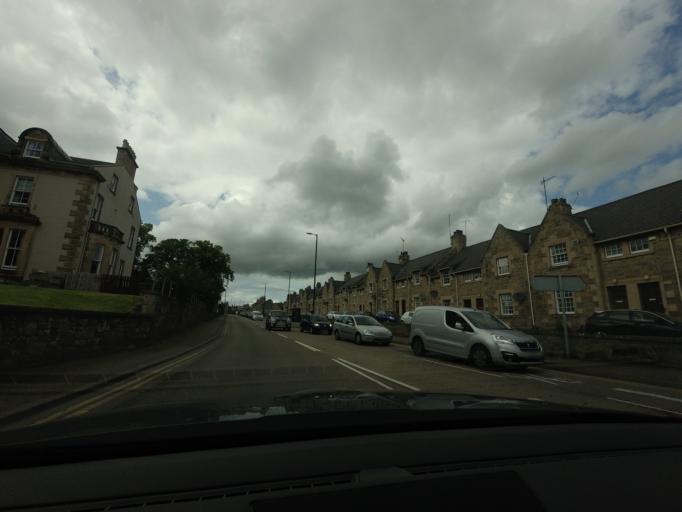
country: GB
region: Scotland
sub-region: Moray
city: Elgin
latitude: 57.6481
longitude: -3.3033
